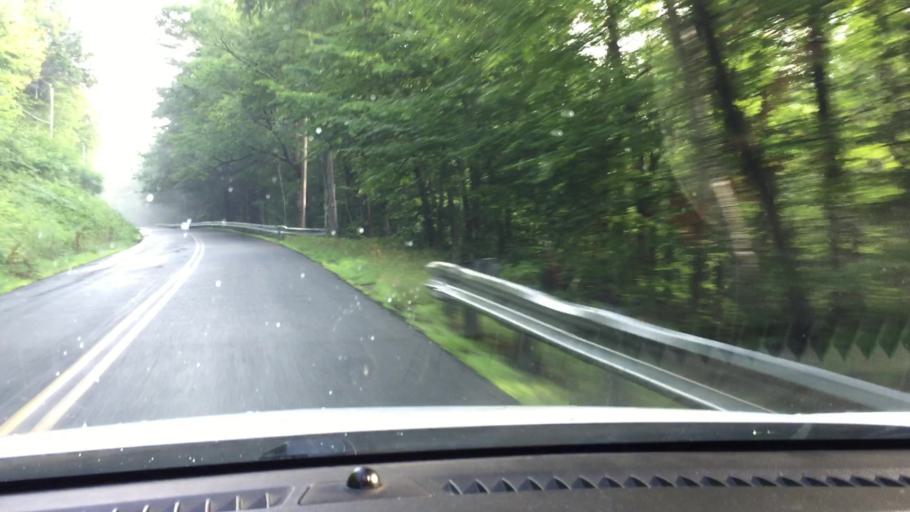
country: US
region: Massachusetts
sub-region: Berkshire County
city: Becket
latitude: 42.4080
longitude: -72.9795
